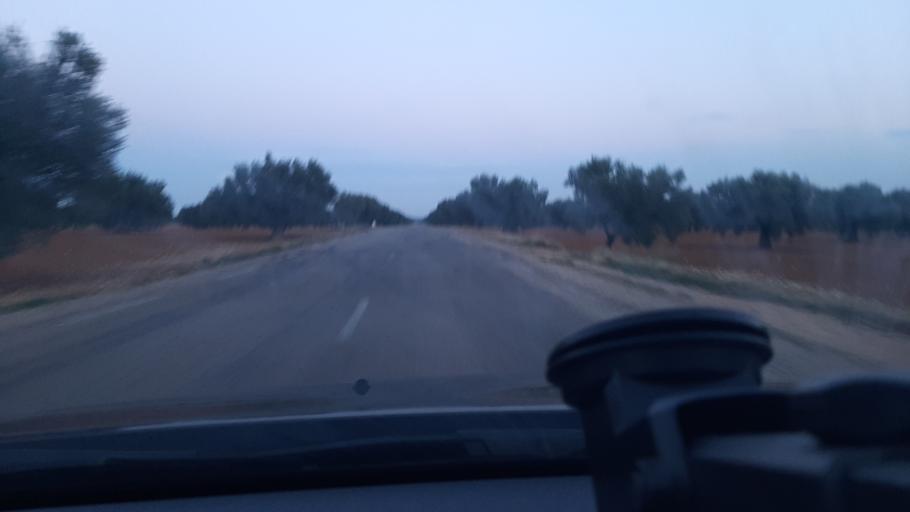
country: TN
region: Al Mahdiyah
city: Shurban
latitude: 35.0316
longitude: 10.4981
